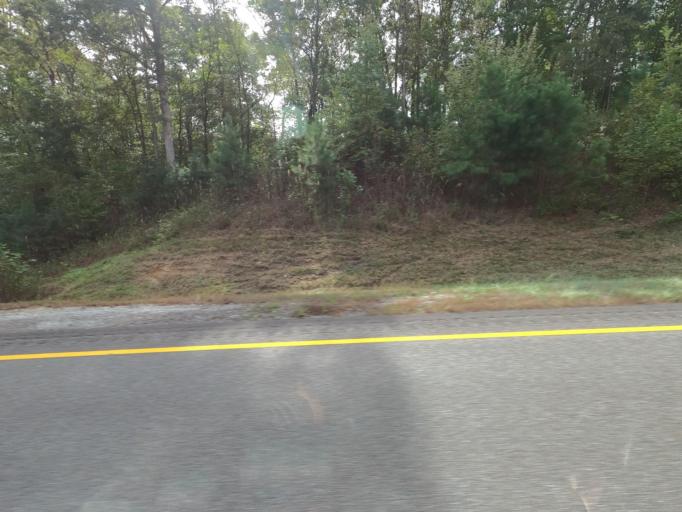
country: US
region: Tennessee
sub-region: Decatur County
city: Parsons
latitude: 35.8158
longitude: -88.2196
